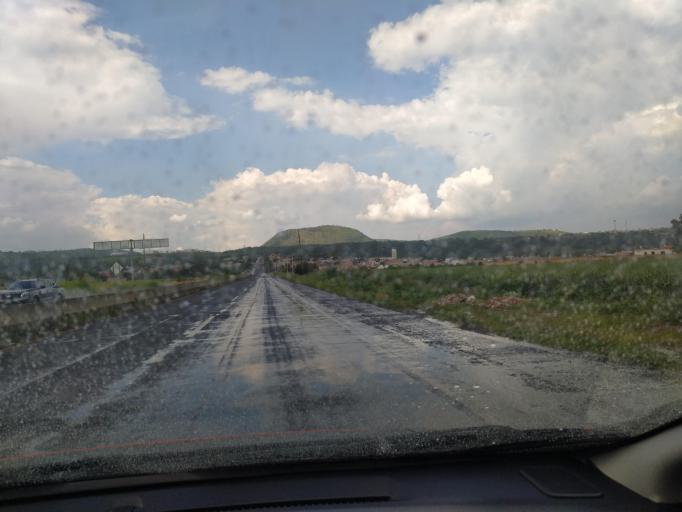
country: MX
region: Jalisco
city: Bellavista
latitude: 20.4242
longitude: -103.6077
